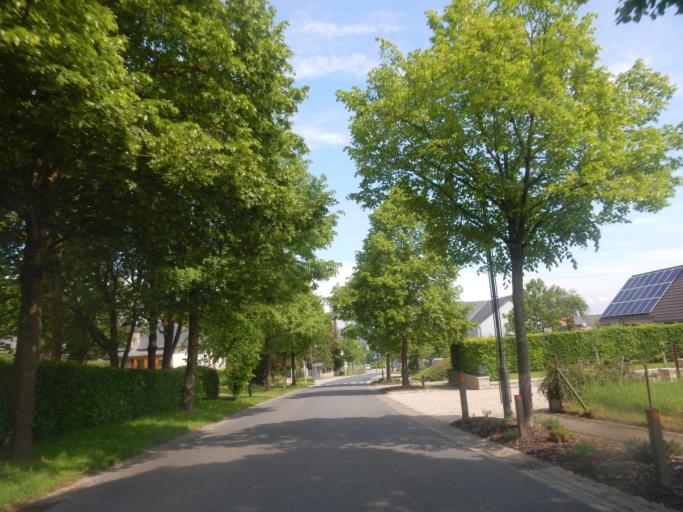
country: LU
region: Luxembourg
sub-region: Canton de Capellen
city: Hobscheid
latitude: 49.7199
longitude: 5.9218
